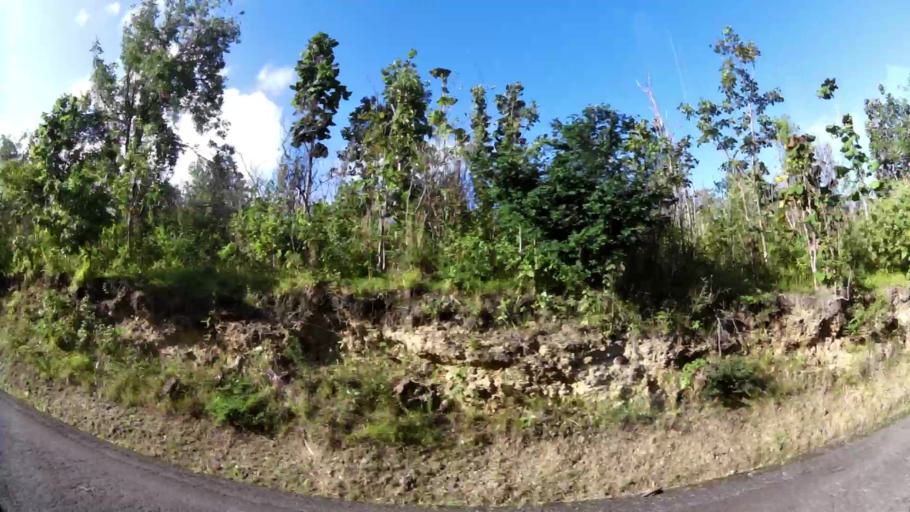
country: LC
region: Anse-la-Raye
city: Anse La Raye
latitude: 13.9226
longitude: -61.0426
